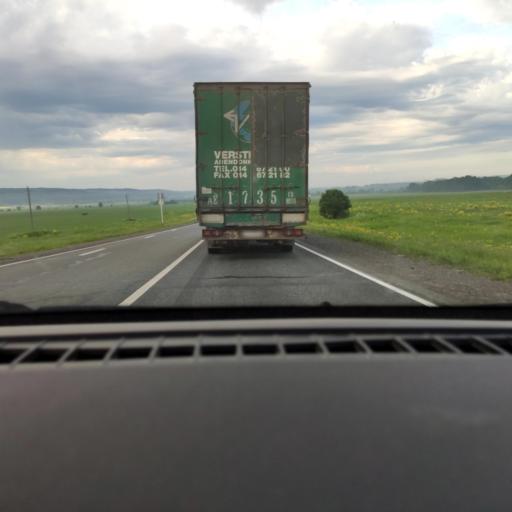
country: RU
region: Perm
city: Chastyye
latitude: 57.4122
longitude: 54.4534
